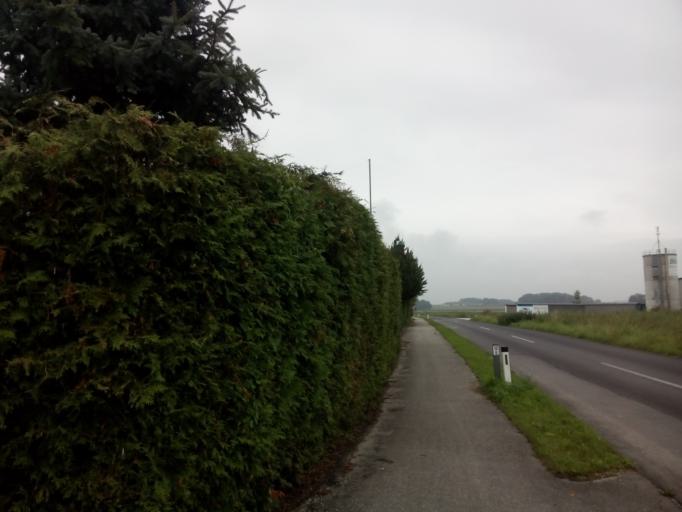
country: AT
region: Upper Austria
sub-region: Wels-Land
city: Sattledt
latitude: 48.0472
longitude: 13.9864
